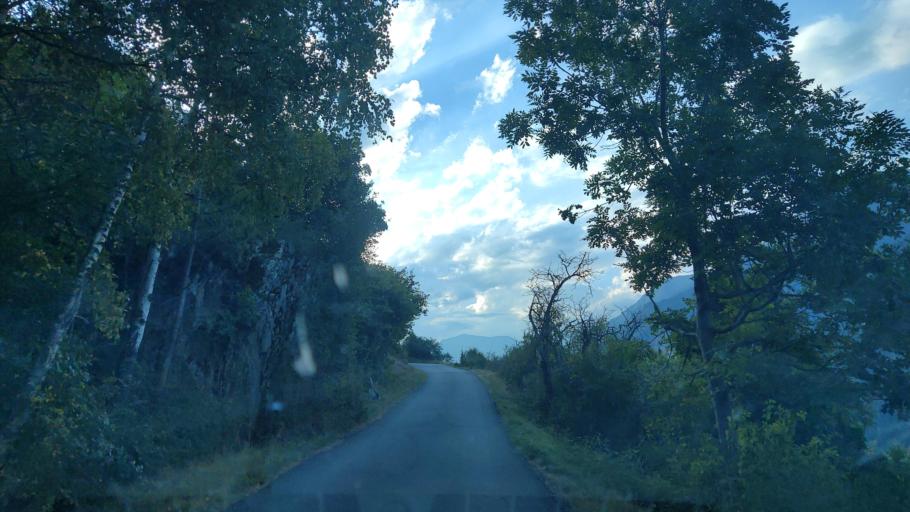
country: FR
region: Rhone-Alpes
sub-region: Departement de la Savoie
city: Val Thorens
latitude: 45.2121
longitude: 6.5655
